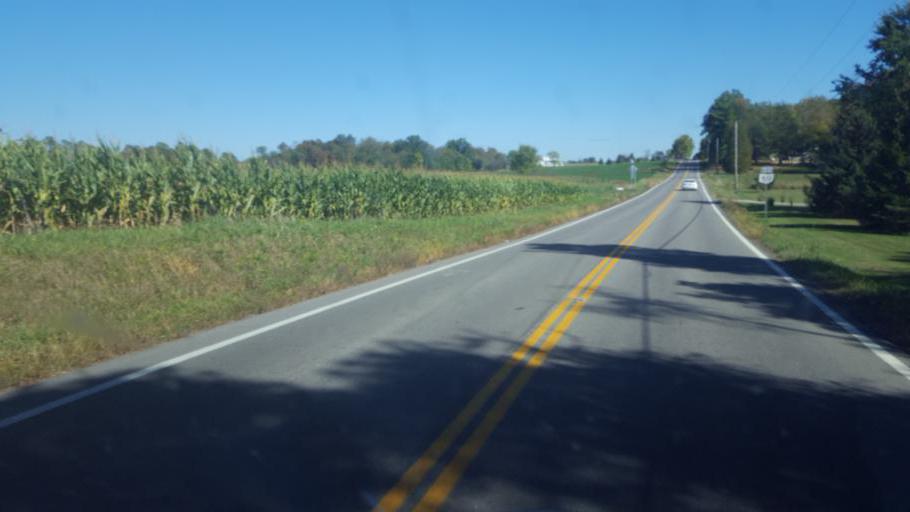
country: US
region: Ohio
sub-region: Ashland County
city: Ashland
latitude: 40.9929
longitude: -82.3107
